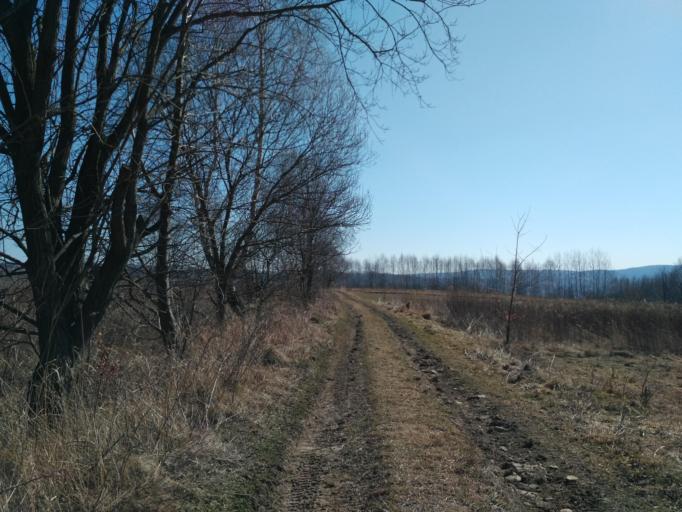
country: PL
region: Subcarpathian Voivodeship
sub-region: Powiat brzozowski
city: Domaradz
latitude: 49.7965
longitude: 21.9725
